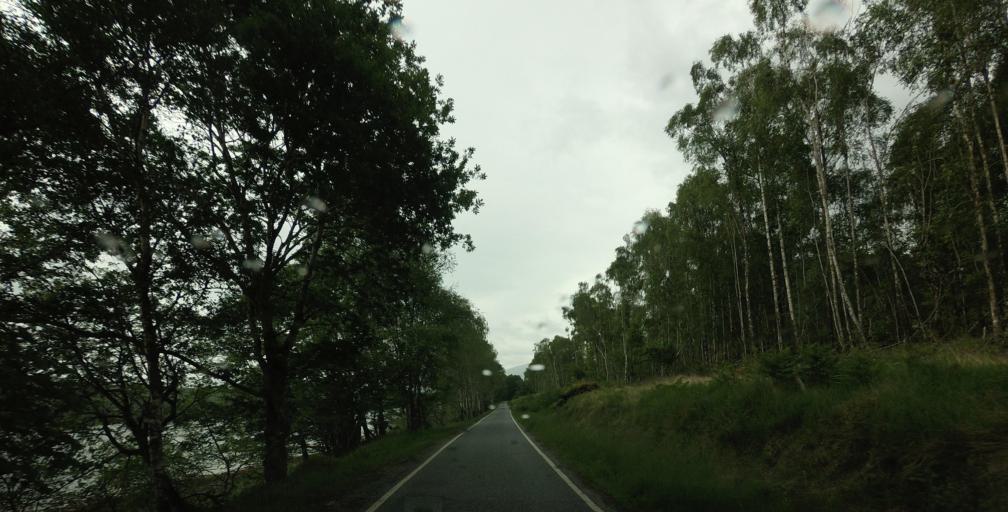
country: GB
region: Scotland
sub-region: Highland
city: Fort William
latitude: 56.8460
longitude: -5.1848
